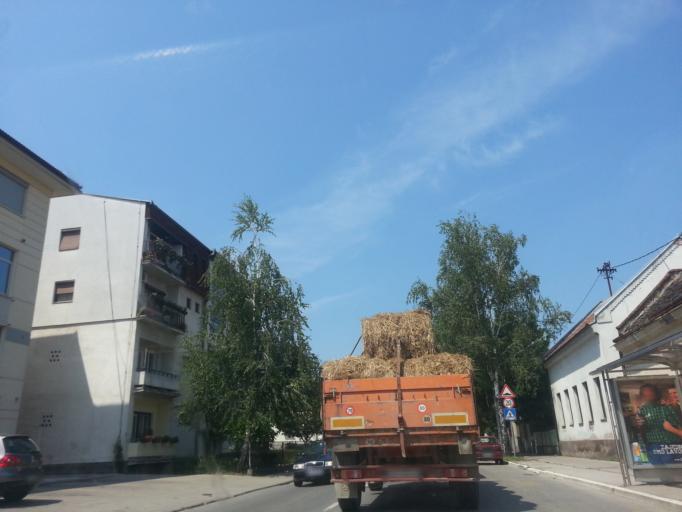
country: BA
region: Brcko
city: Brcko
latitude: 44.8685
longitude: 18.8106
